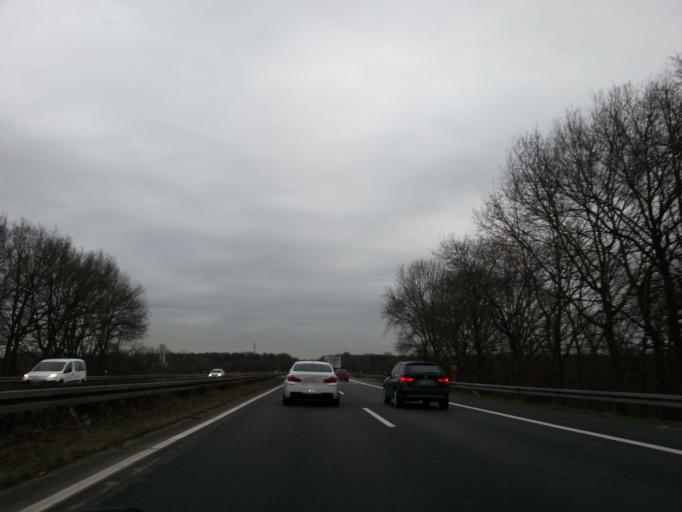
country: DE
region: North Rhine-Westphalia
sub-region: Regierungsbezirk Dusseldorf
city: Hunxe
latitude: 51.6479
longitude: 6.7385
